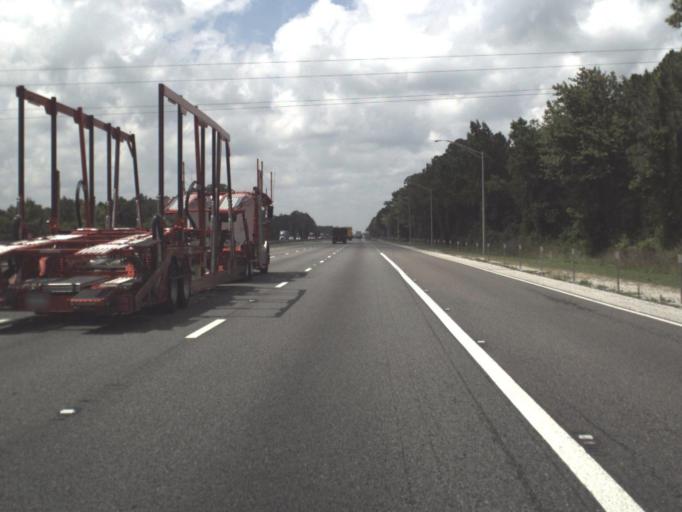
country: US
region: Florida
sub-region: Saint Johns County
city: Saint Augustine Shores
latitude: 29.7045
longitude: -81.3289
